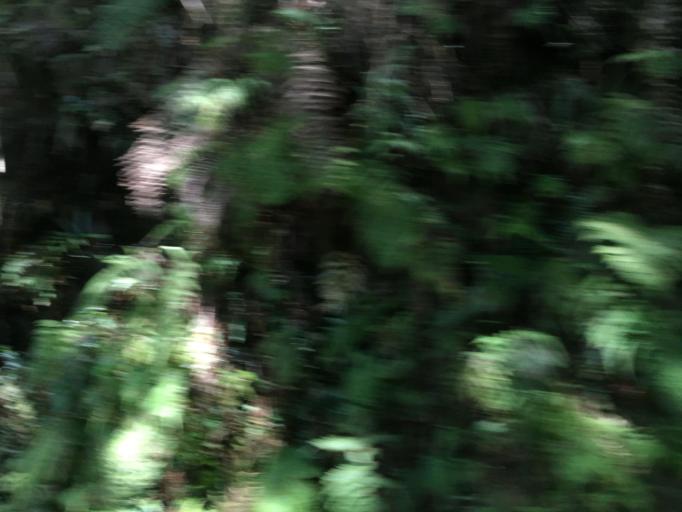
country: TW
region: Taiwan
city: Daxi
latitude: 24.5897
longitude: 121.4104
